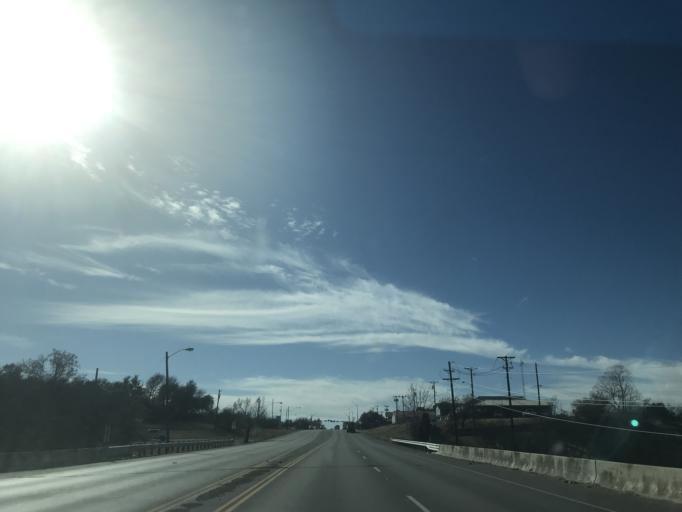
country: US
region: Texas
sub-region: Erath County
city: Stephenville
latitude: 32.2090
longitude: -98.2019
